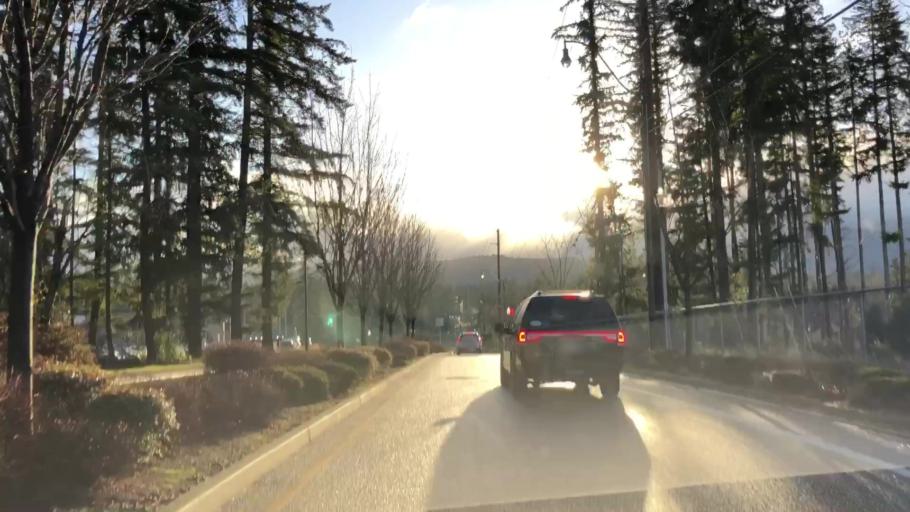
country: US
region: Washington
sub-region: King County
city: City of Sammamish
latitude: 47.5804
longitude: -122.0309
